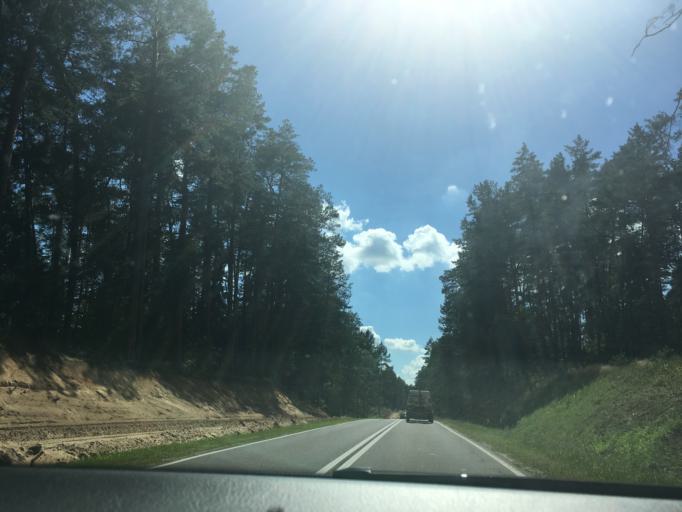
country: PL
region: Podlasie
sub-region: Powiat augustowski
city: Augustow
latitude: 53.8512
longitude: 23.0501
